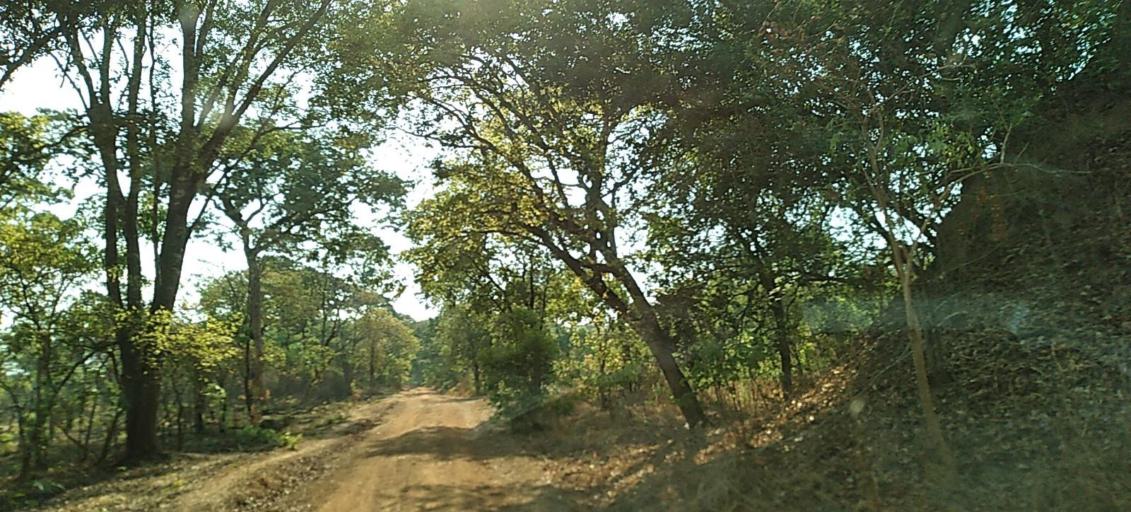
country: ZM
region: Copperbelt
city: Kalulushi
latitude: -13.0070
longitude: 27.7226
